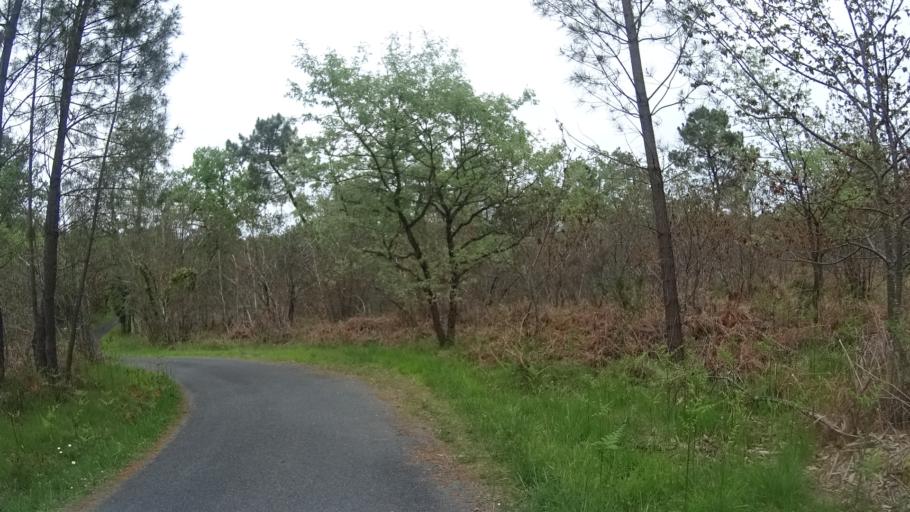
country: FR
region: Aquitaine
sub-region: Departement de la Dordogne
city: Lembras
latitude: 44.9676
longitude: 0.5044
